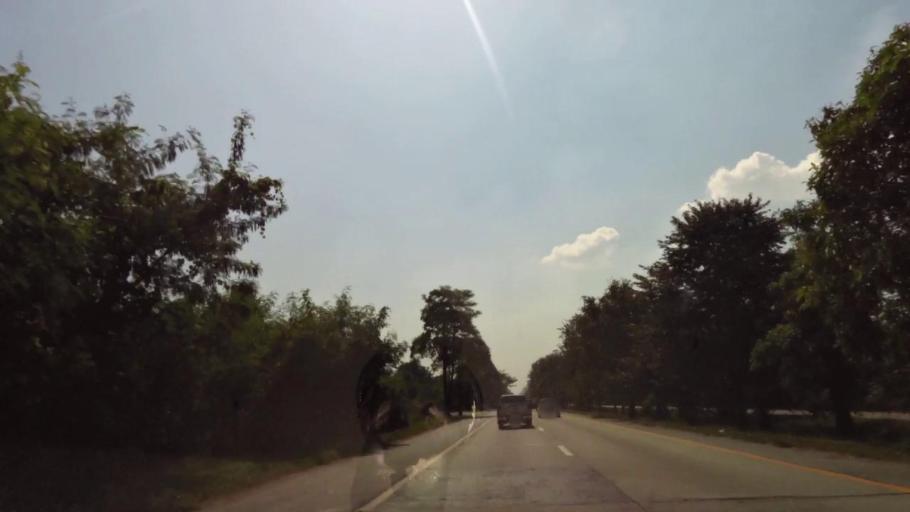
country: TH
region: Phichit
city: Wachira Barami
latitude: 16.5584
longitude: 100.1479
